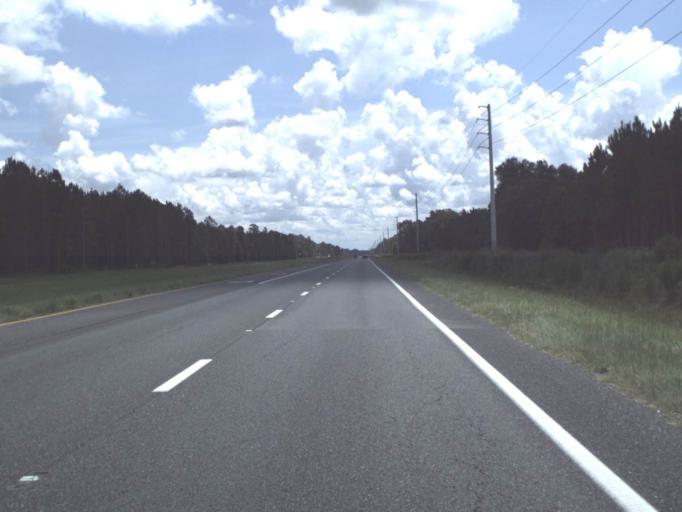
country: US
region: Florida
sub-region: Levy County
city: Bronson
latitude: 29.4758
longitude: -82.7222
